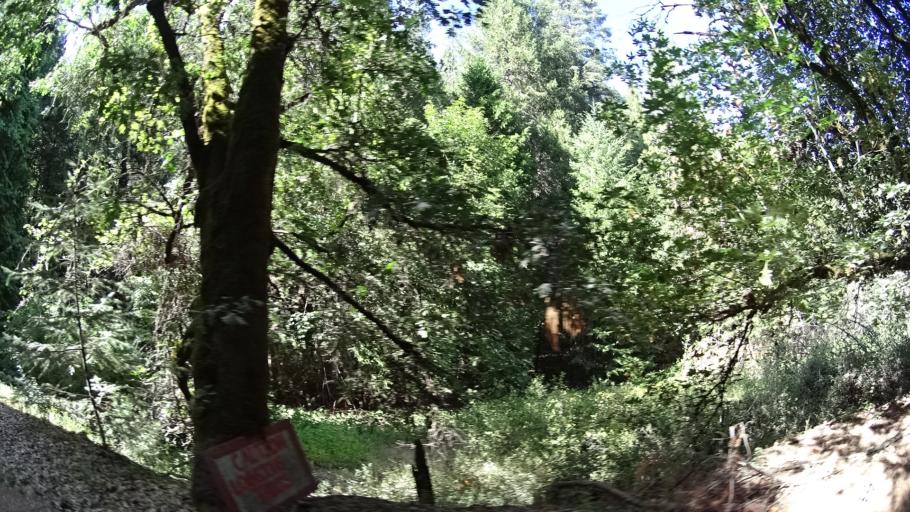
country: US
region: California
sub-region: Calaveras County
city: Arnold
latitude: 38.3668
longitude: -120.4380
